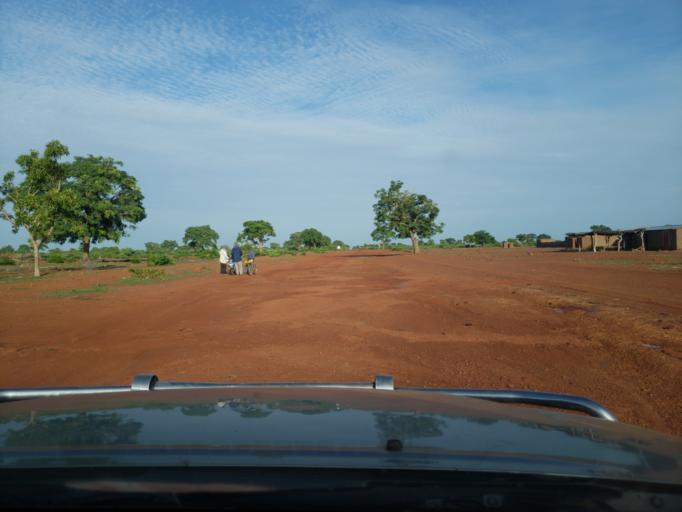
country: ML
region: Sikasso
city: Koutiala
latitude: 12.4286
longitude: -5.6225
